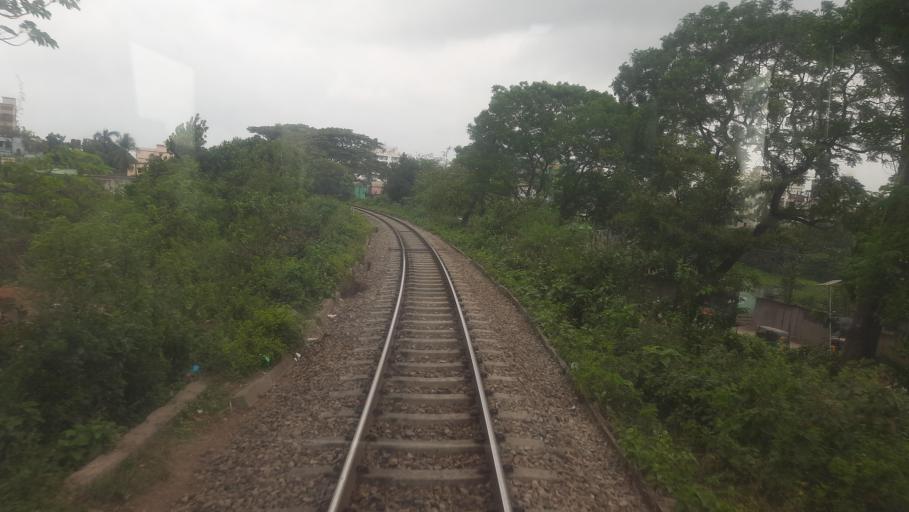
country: BD
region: Dhaka
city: Bhairab Bazar
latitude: 24.0505
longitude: 90.9885
